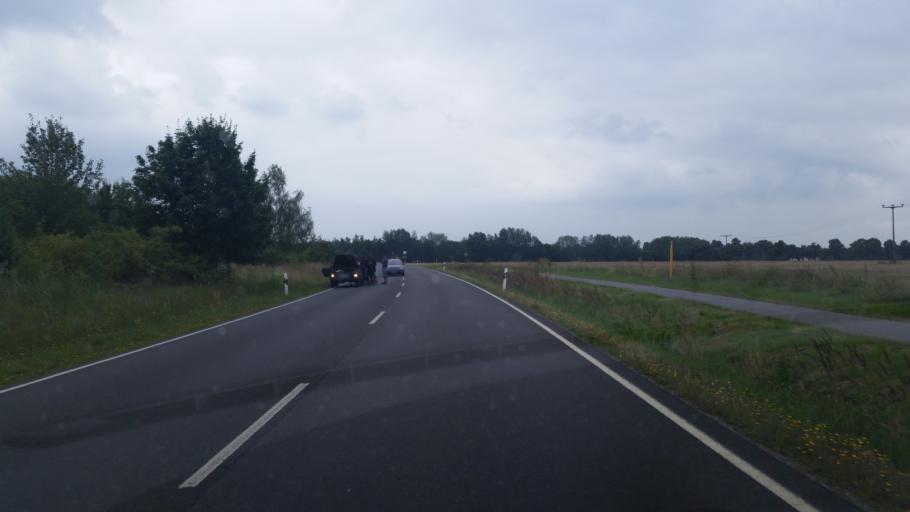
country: DE
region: Brandenburg
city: Hohenbocka
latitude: 51.4746
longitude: 14.0684
